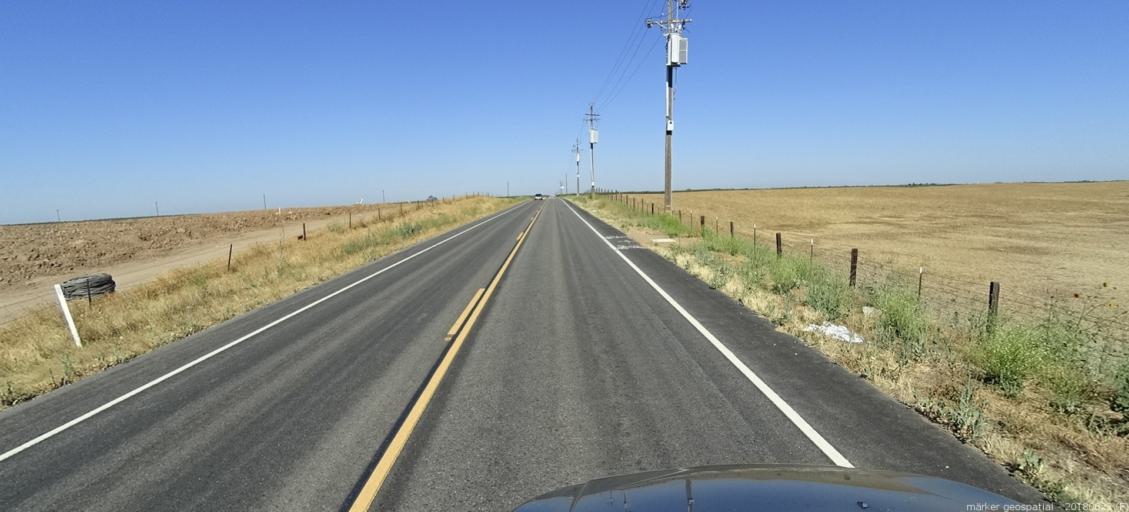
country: US
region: California
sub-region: Madera County
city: Bonadelle Ranchos-Madera Ranchos
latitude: 36.9666
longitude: -119.9351
